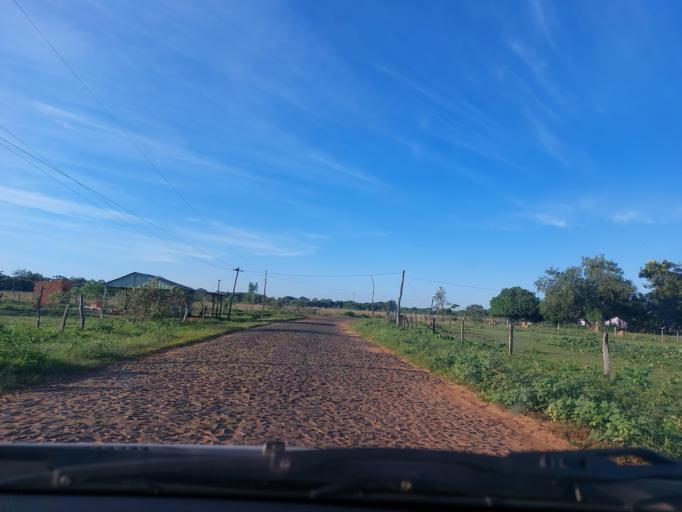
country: PY
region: San Pedro
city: Itacurubi del Rosario
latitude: -24.5827
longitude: -56.6002
